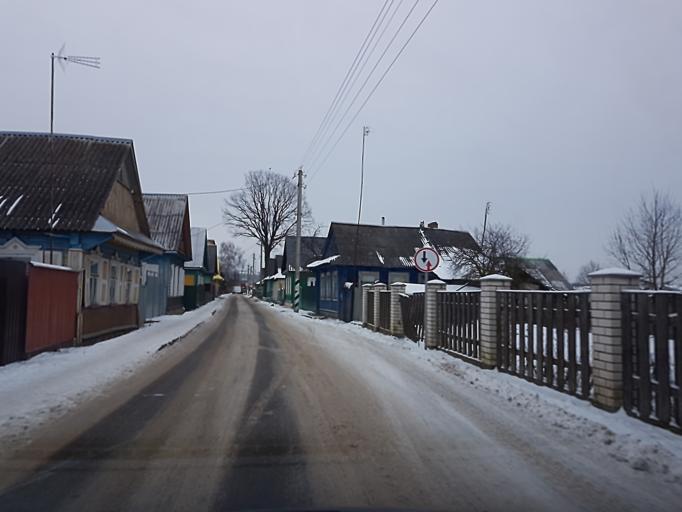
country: BY
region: Minsk
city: Rakaw
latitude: 53.9681
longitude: 27.0582
